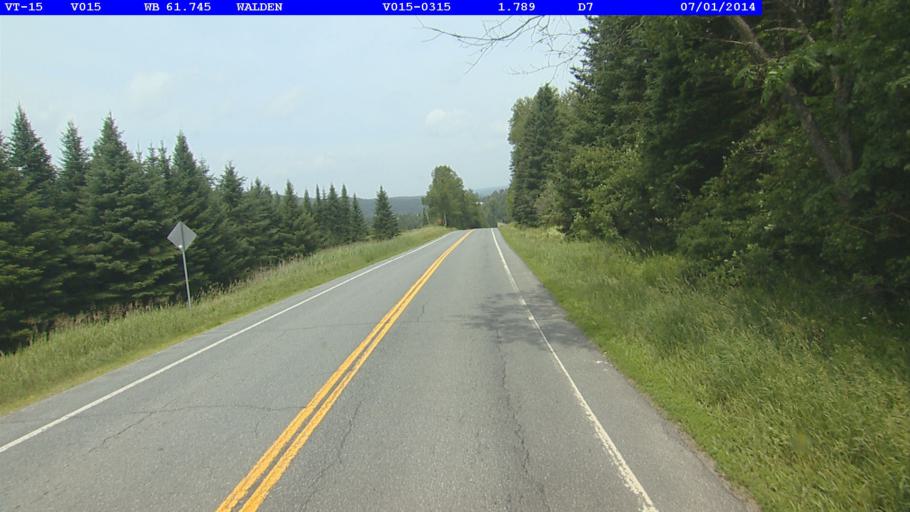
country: US
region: Vermont
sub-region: Caledonia County
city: Hardwick
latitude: 44.4693
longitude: -72.2781
